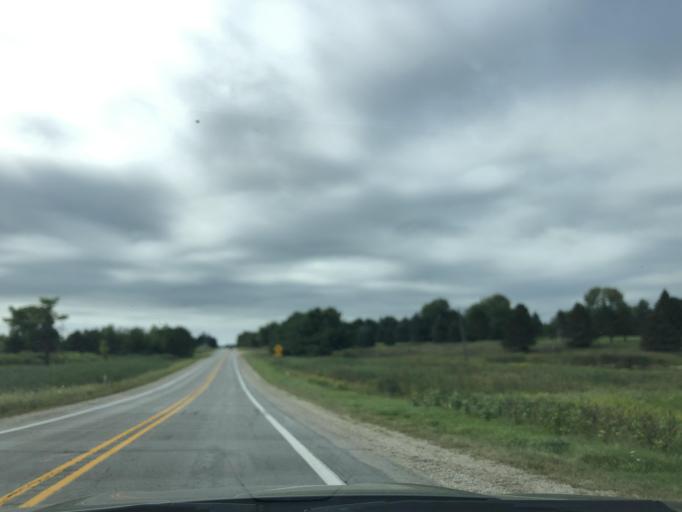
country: US
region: Michigan
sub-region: Missaukee County
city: Lake City
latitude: 44.2621
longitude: -85.2152
